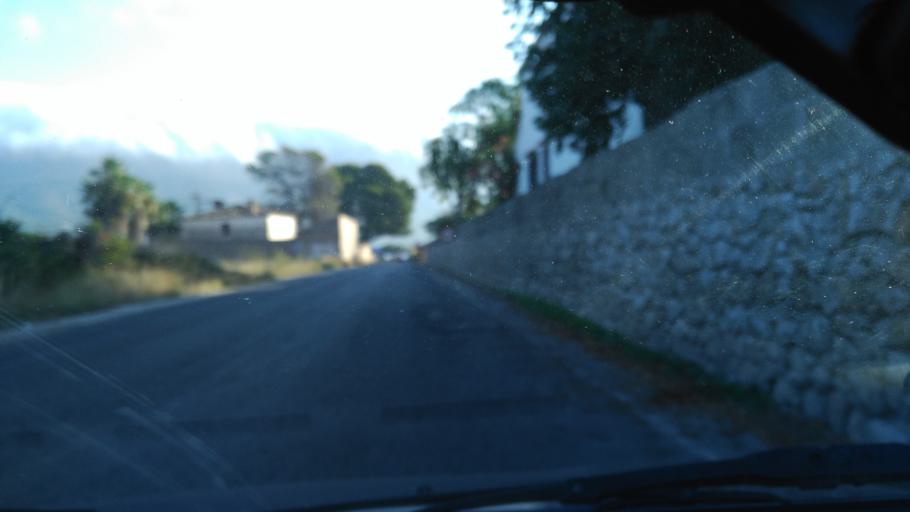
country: ES
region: Valencia
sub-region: Provincia de Alicante
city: Gata de Gorgos
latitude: 38.7817
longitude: 0.0895
